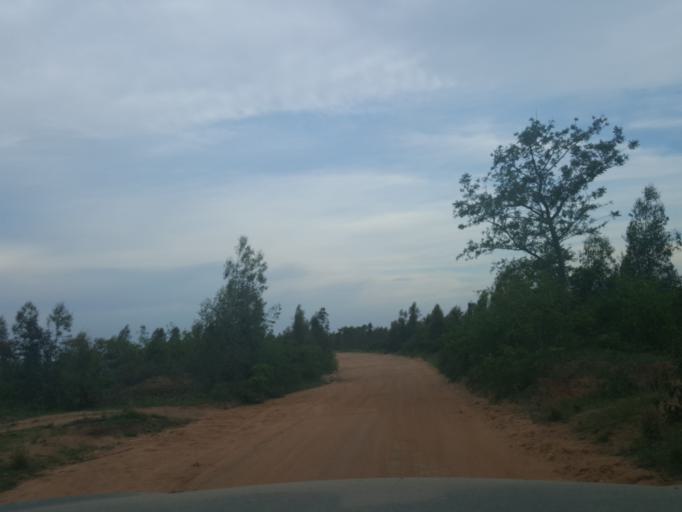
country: ZA
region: Limpopo
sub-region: Mopani District Municipality
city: Hoedspruit
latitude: -24.5879
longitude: 30.9630
